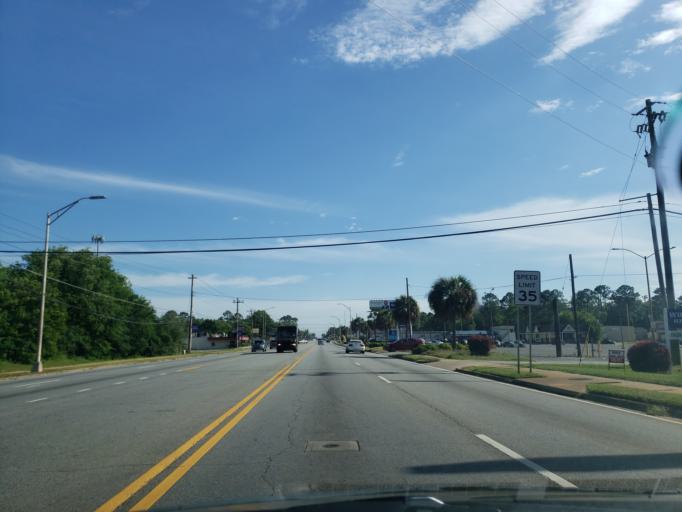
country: US
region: Georgia
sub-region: Dougherty County
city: Albany
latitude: 31.6045
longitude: -84.1759
